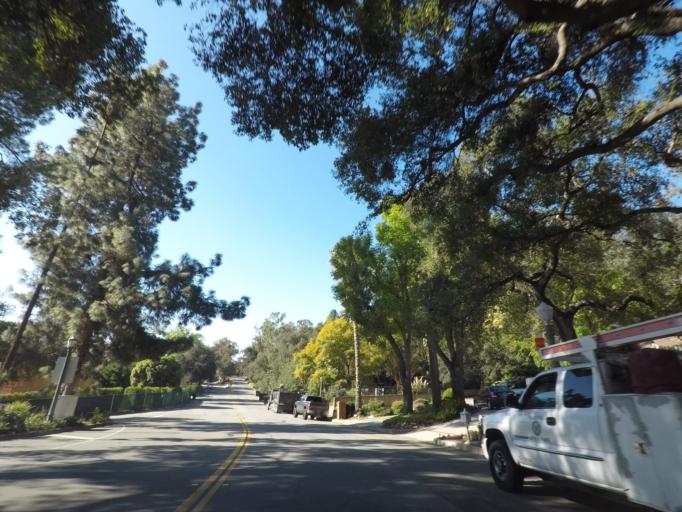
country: US
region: California
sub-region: Los Angeles County
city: Pasadena
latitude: 34.1473
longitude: -118.1672
